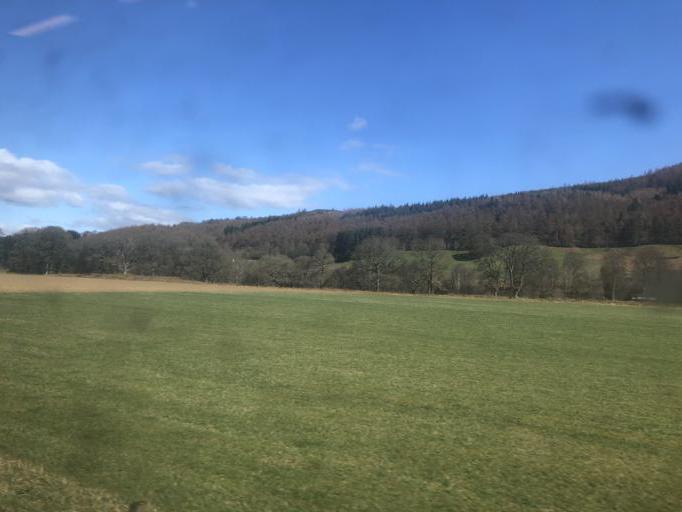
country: GB
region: Scotland
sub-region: Perth and Kinross
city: Bankfoot
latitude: 56.5845
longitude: -3.6273
